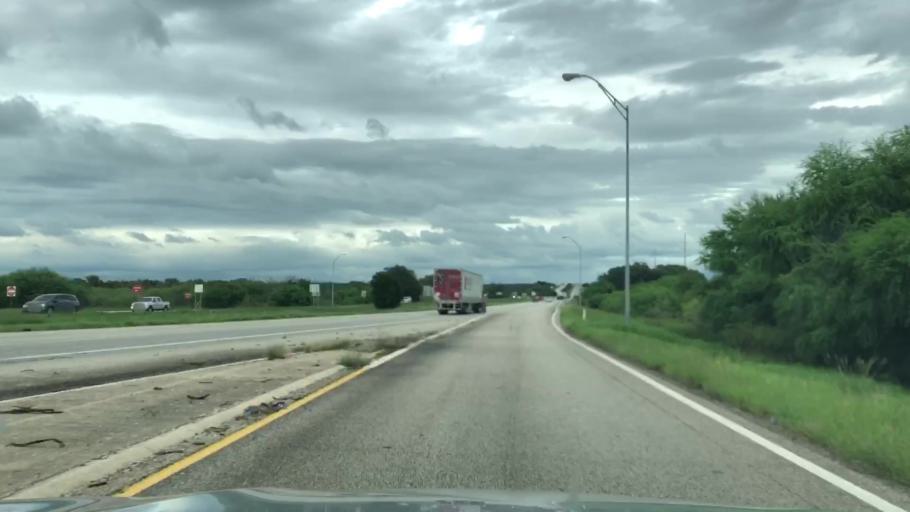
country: US
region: Texas
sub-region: Guadalupe County
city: Seguin
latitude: 29.5992
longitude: -97.9469
